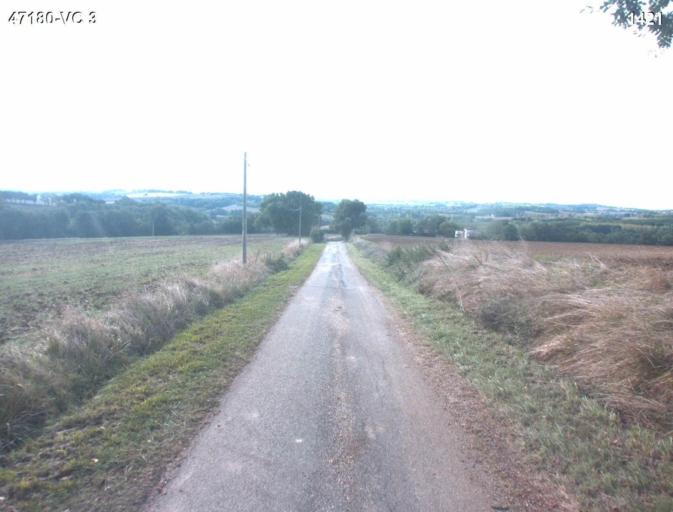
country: FR
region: Aquitaine
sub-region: Departement du Lot-et-Garonne
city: Sainte-Colombe-en-Bruilhois
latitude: 44.1567
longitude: 0.4425
